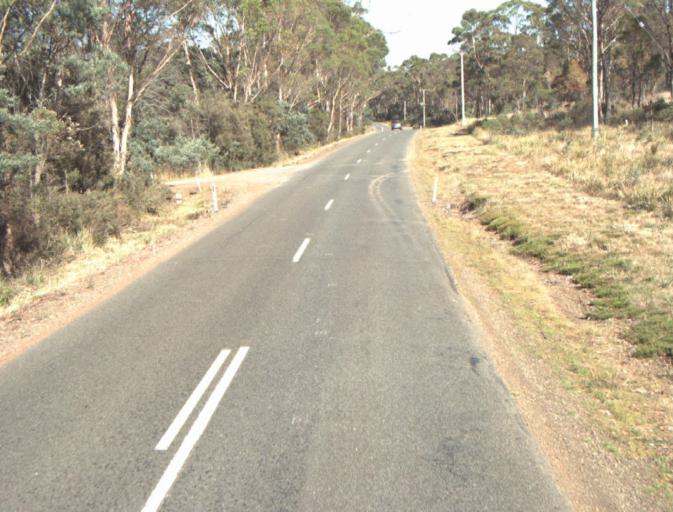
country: AU
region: Tasmania
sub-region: Launceston
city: Mayfield
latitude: -41.3303
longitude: 147.1404
